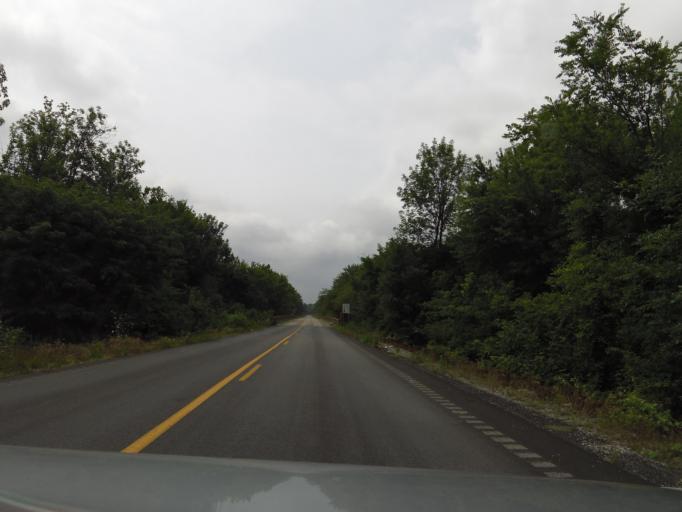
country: US
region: Kentucky
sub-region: Hopkins County
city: Madisonville
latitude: 37.3150
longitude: -87.3683
